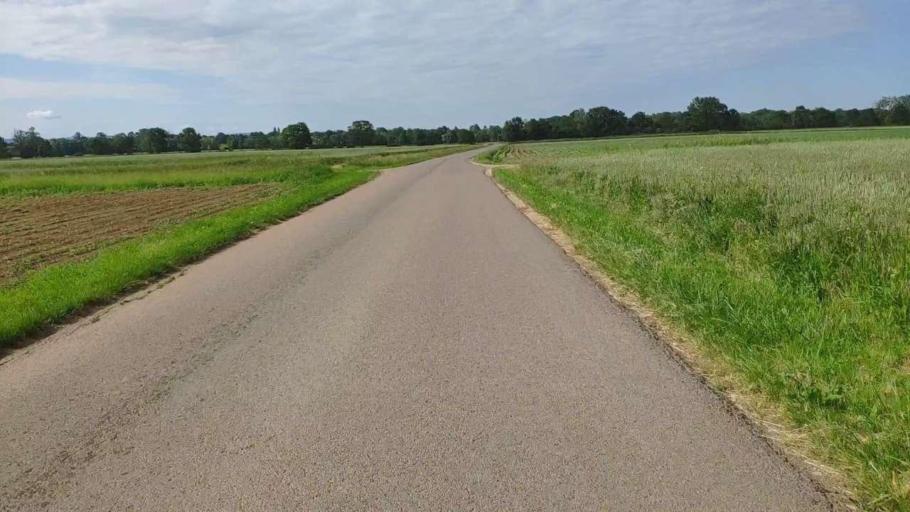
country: FR
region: Franche-Comte
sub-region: Departement du Jura
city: Bletterans
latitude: 46.7266
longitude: 5.4634
